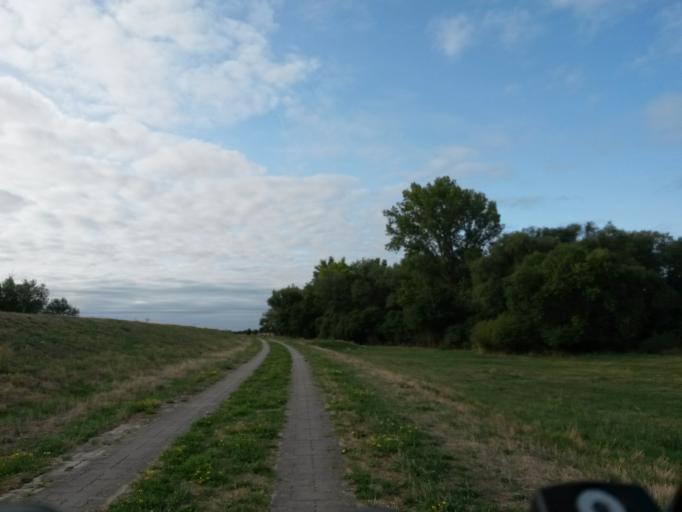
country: DE
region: Saxony-Anhalt
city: Tangermunde
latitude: 52.5045
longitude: 11.9577
